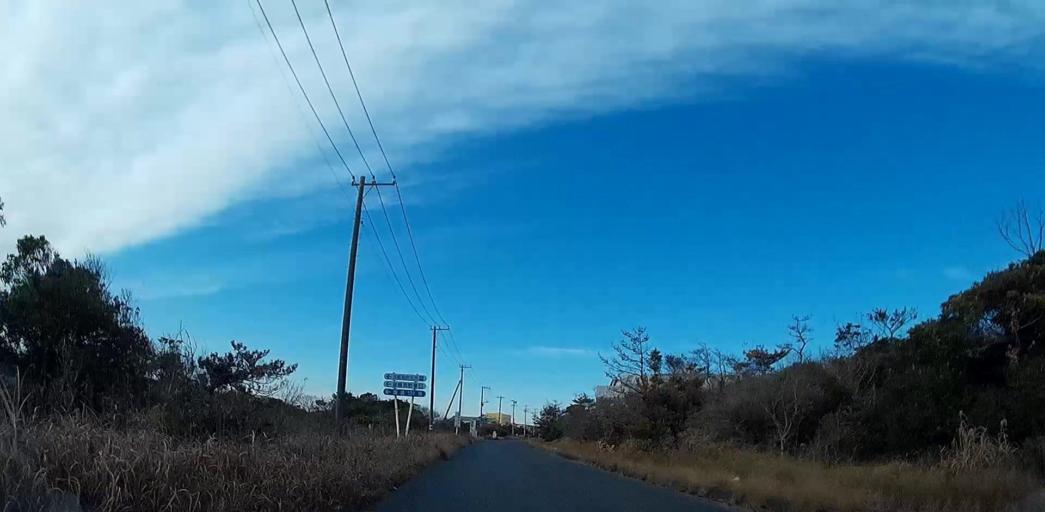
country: JP
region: Chiba
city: Hasaki
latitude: 35.7654
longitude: 140.8186
